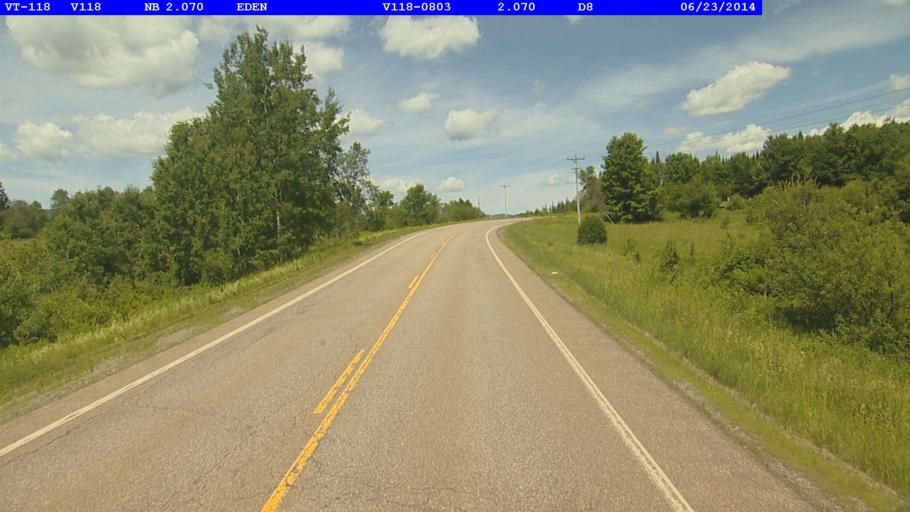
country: US
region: Vermont
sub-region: Lamoille County
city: Hyde Park
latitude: 44.7330
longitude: -72.5659
